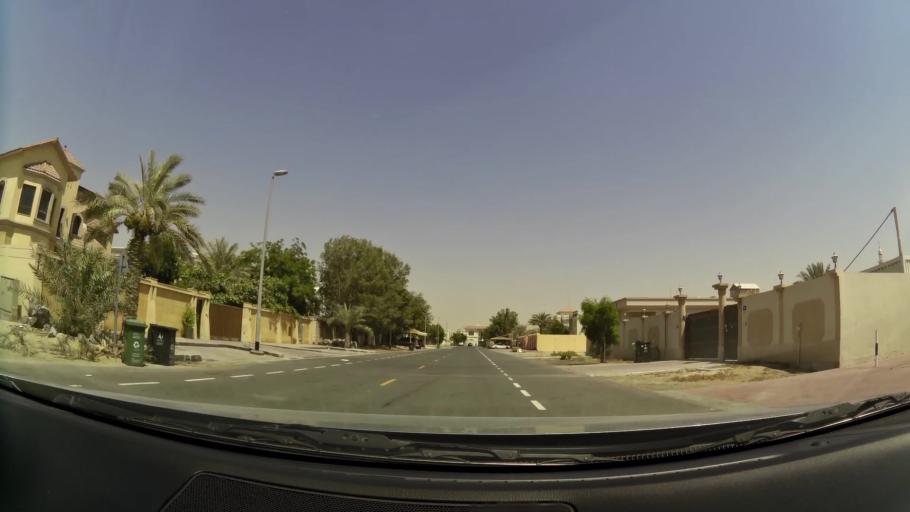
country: AE
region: Dubai
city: Dubai
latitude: 25.1040
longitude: 55.2117
